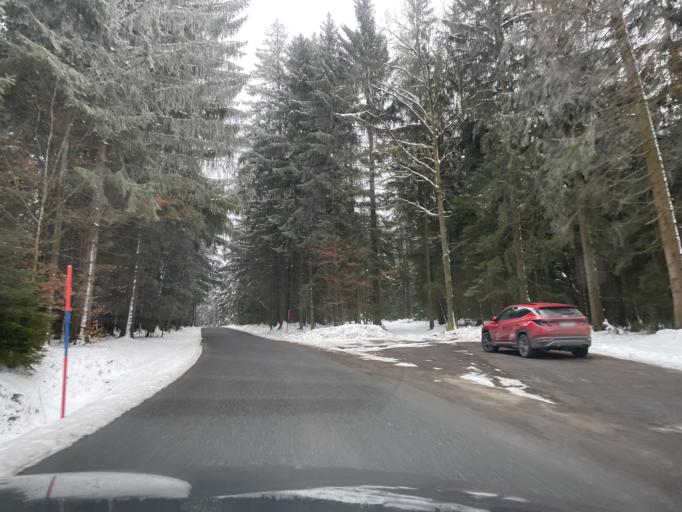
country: DE
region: Bavaria
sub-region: Lower Bavaria
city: Viechtach
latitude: 49.1369
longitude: 12.9096
